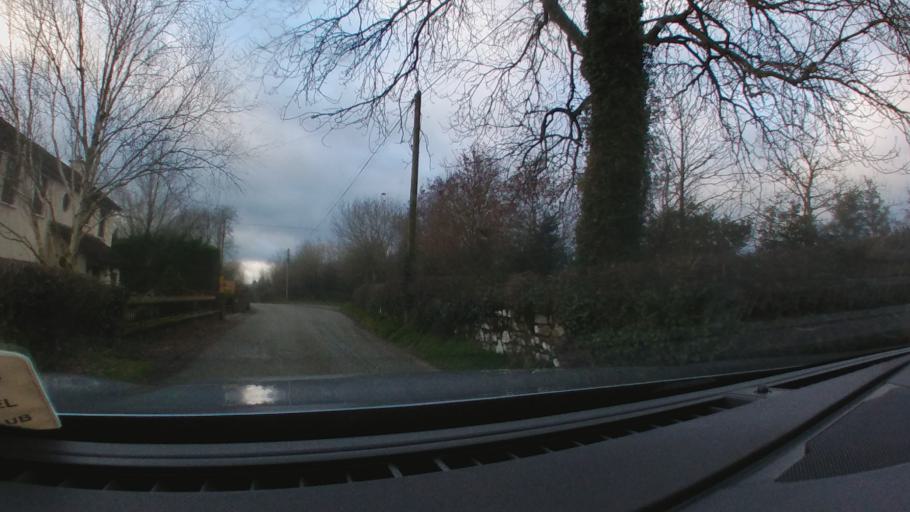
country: IE
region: Leinster
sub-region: Kilkenny
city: Thomastown
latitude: 52.5873
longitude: -7.1722
